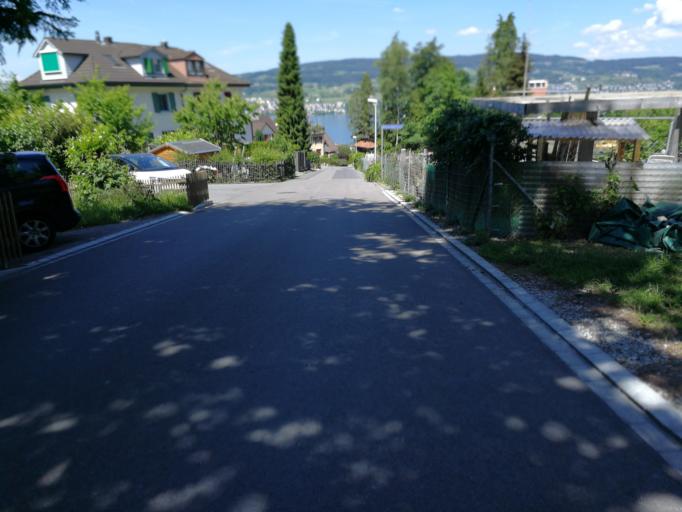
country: CH
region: Zurich
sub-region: Bezirk Horgen
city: Horgen / Allmend
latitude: 47.2515
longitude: 8.6099
